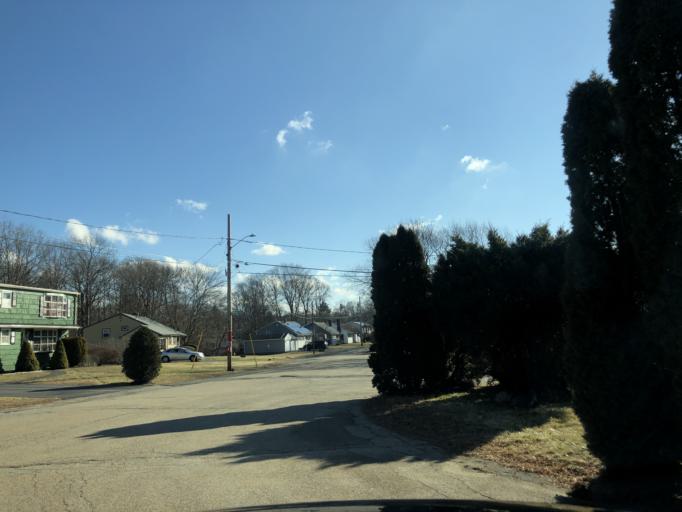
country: US
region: Massachusetts
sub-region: Norfolk County
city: Avon
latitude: 42.1152
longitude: -71.0138
